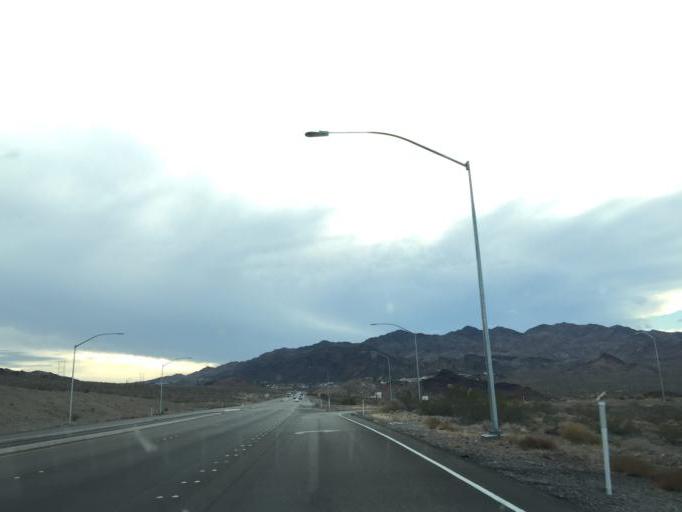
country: US
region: Nevada
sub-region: Clark County
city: Boulder City
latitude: 36.0093
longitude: -114.7990
